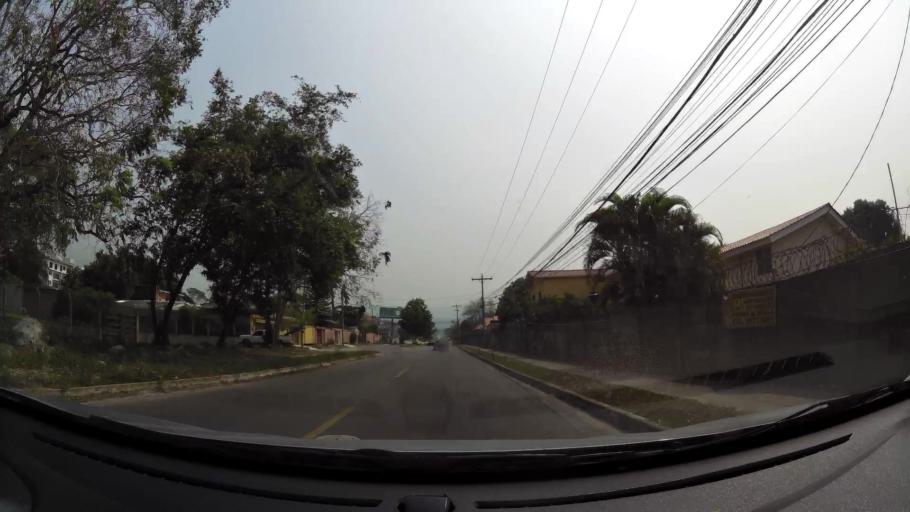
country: HN
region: Cortes
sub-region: San Pedro Sula
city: Pena Blanca
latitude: 15.5648
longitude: -88.0296
